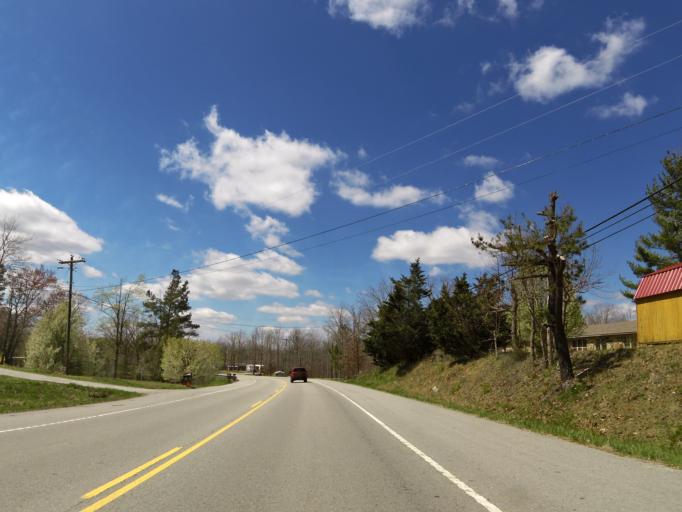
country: US
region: Tennessee
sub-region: White County
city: Sparta
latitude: 35.9540
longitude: -85.3010
